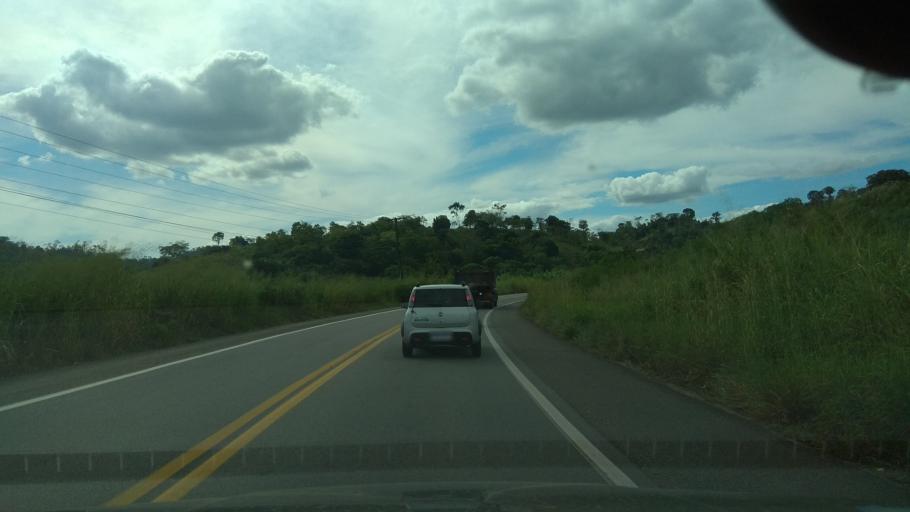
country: BR
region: Bahia
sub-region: Ipiau
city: Ipiau
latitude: -14.1039
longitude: -39.7772
